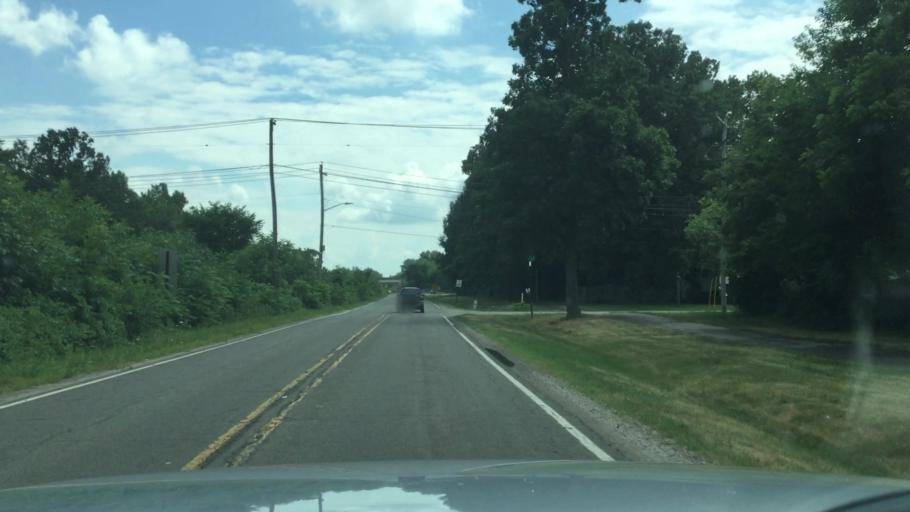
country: US
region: Michigan
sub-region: Washtenaw County
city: Ypsilanti
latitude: 42.2251
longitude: -83.5629
